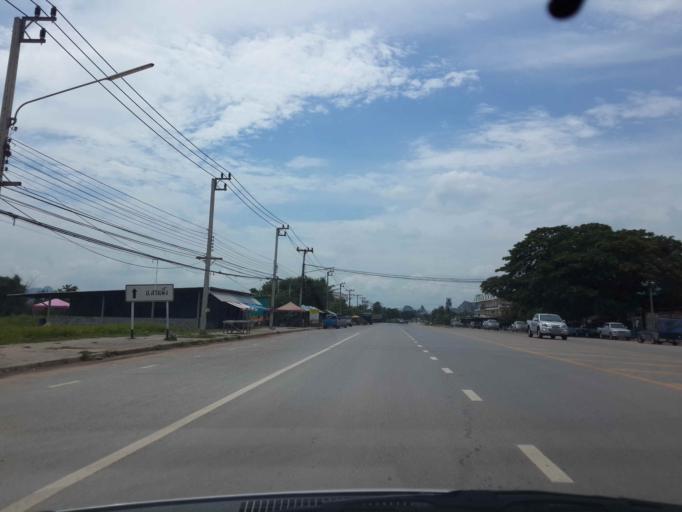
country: TH
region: Ratchaburi
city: Pak Tho
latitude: 13.3671
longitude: 99.8196
